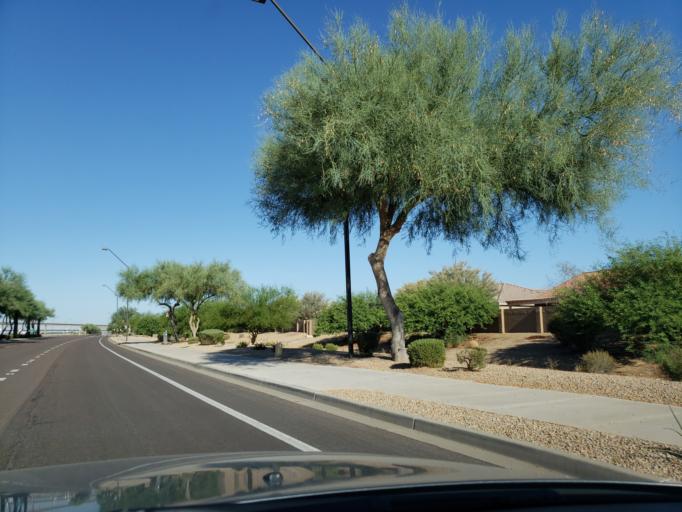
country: US
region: Arizona
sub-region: Maricopa County
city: Litchfield Park
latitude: 33.4648
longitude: -112.4149
